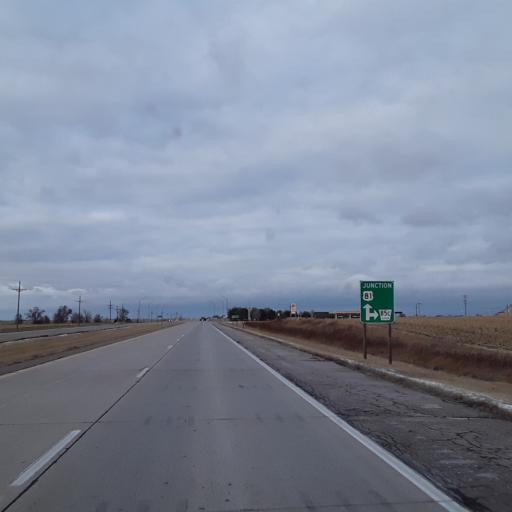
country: US
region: Nebraska
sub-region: Thayer County
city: Hebron
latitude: 40.3322
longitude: -97.5766
